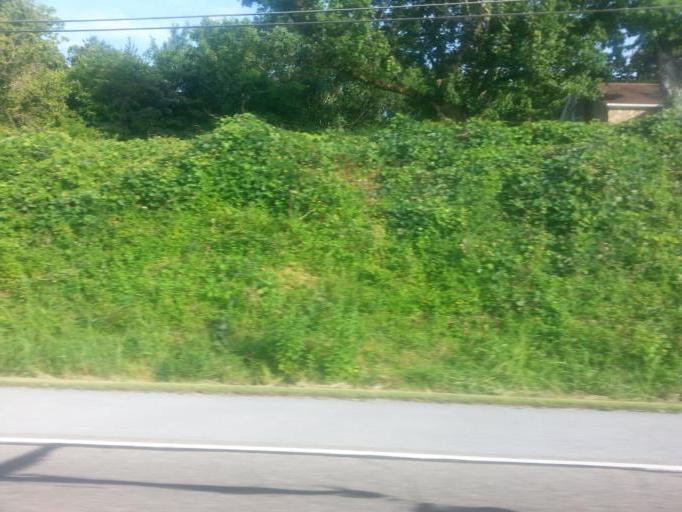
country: US
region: Tennessee
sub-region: Sevier County
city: Sevierville
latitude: 35.8721
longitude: -83.5932
